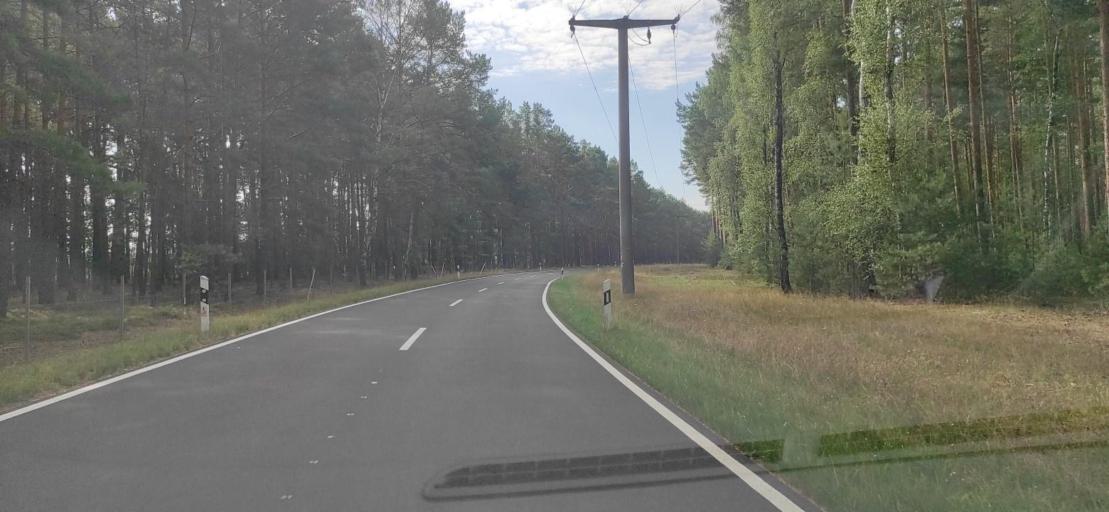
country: PL
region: Lubusz
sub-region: Powiat zarski
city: Trzebiel
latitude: 51.6547
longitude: 14.7453
